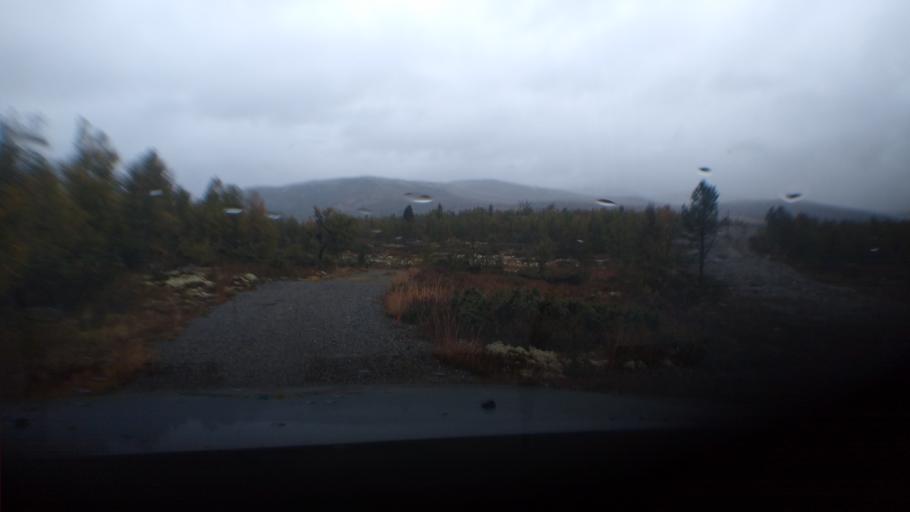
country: NO
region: Oppland
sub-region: Ringebu
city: Ringebu
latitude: 61.6625
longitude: 10.1033
